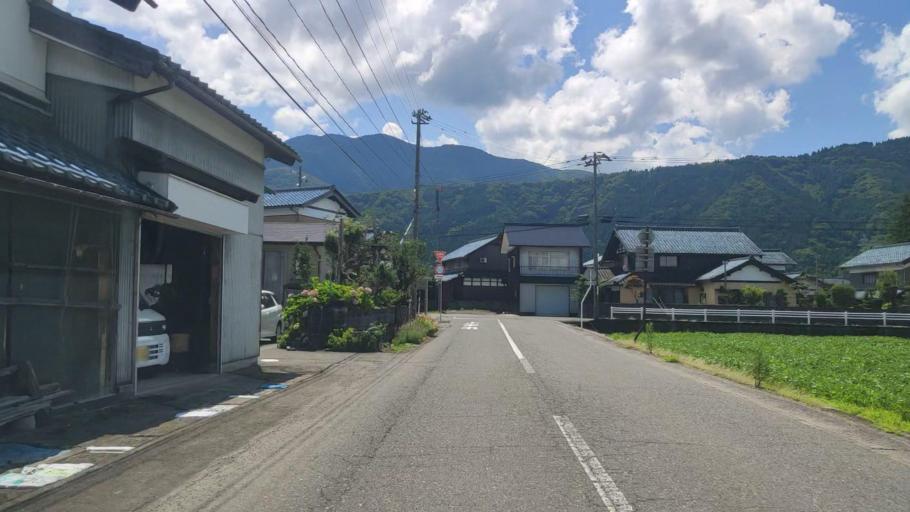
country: JP
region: Fukui
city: Ono
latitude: 35.9432
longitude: 136.5453
